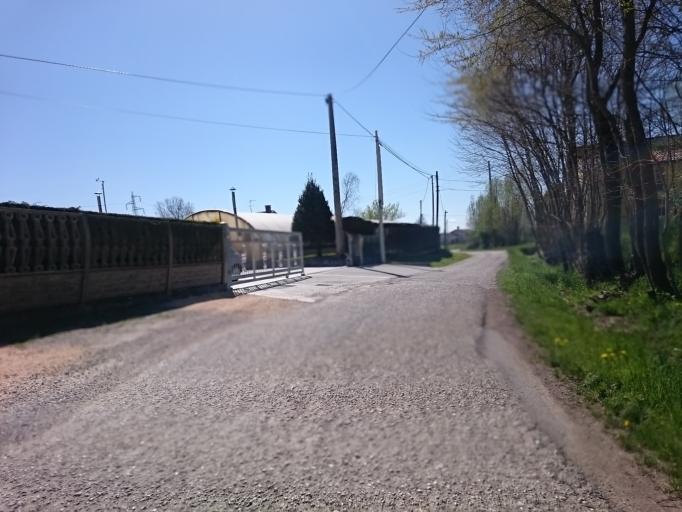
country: IT
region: Veneto
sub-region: Provincia di Padova
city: Polverara
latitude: 45.3122
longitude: 11.9721
